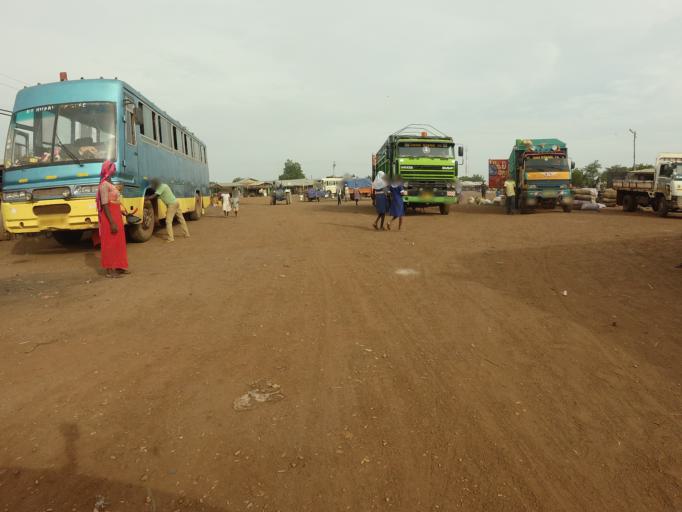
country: GH
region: Northern
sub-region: Yendi
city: Yendi
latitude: 9.9235
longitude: -0.2185
